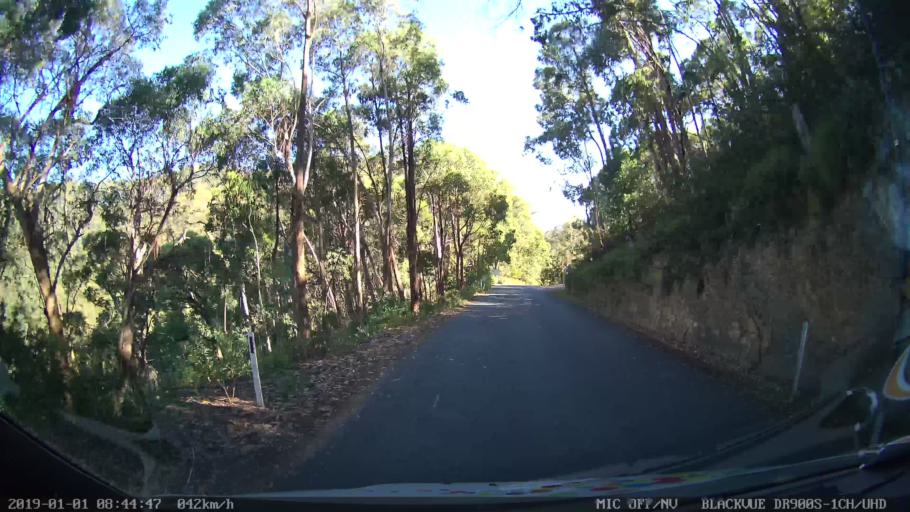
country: AU
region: New South Wales
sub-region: Snowy River
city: Jindabyne
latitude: -36.3094
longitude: 148.1878
